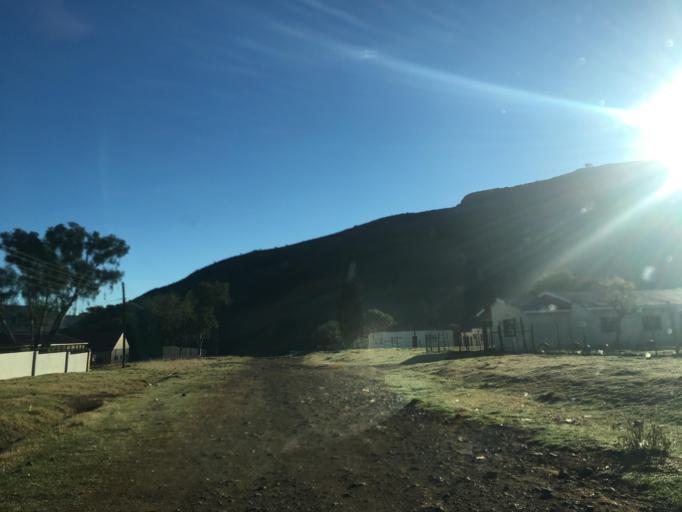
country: ZA
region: Eastern Cape
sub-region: Chris Hani District Municipality
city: Cala
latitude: -31.5272
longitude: 27.7022
